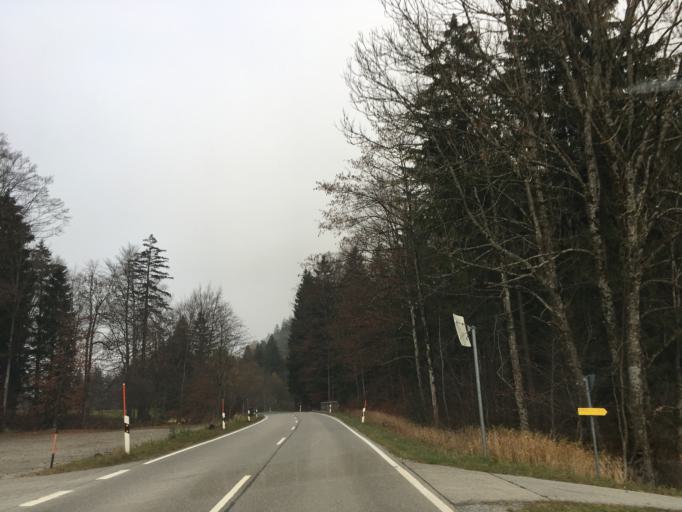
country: AT
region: Tyrol
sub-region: Politischer Bezirk Kufstein
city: Rettenschoss
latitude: 47.7100
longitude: 12.2835
